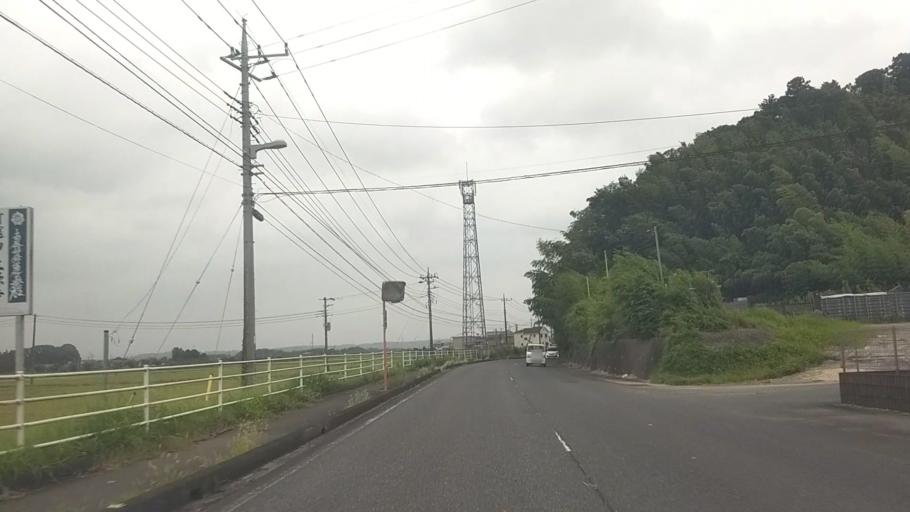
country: JP
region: Chiba
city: Kisarazu
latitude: 35.3768
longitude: 140.0184
